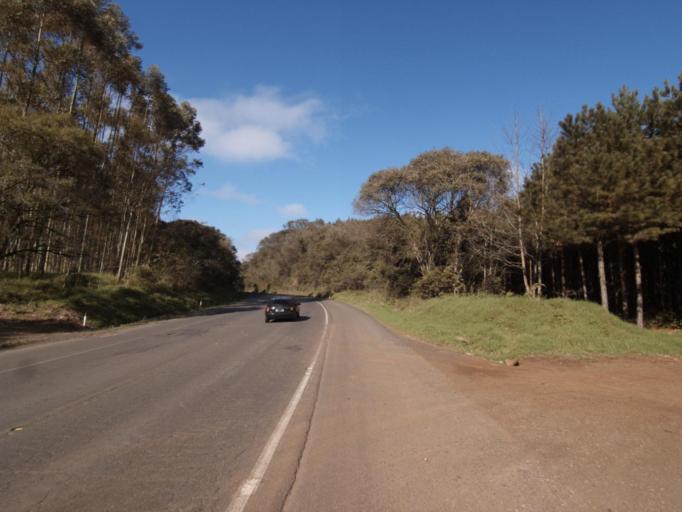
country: BR
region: Rio Grande do Sul
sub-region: Frederico Westphalen
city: Frederico Westphalen
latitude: -27.0491
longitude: -53.2296
